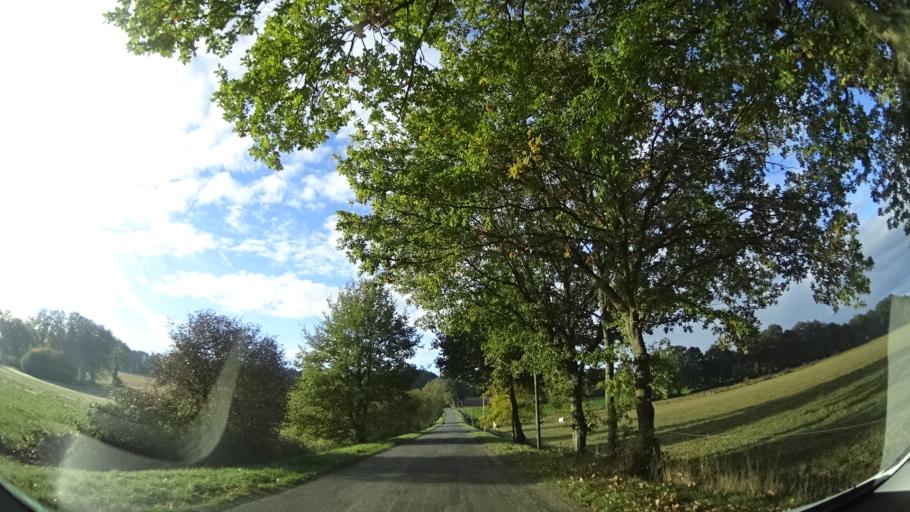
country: FR
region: Brittany
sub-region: Departement d'Ille-et-Vilaine
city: Geveze
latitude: 48.2157
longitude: -1.7948
